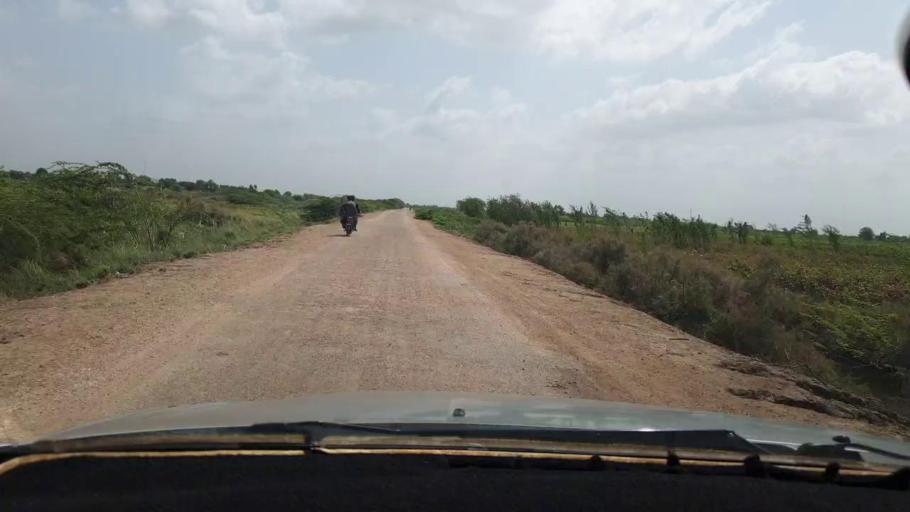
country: PK
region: Sindh
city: Tando Bago
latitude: 24.7205
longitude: 69.1884
